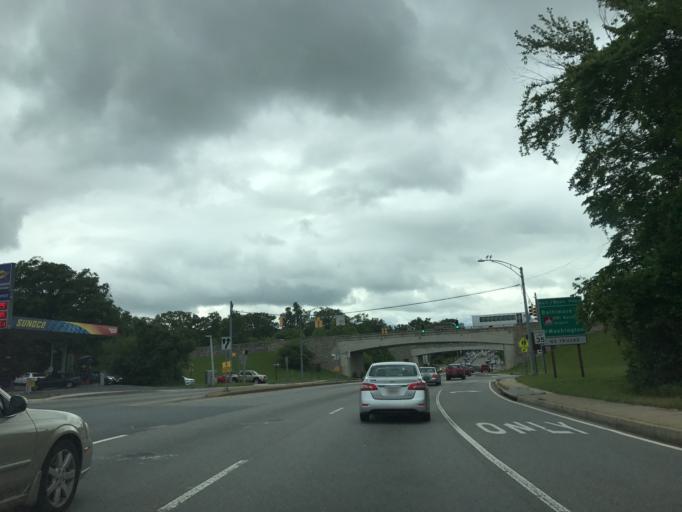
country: US
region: Maryland
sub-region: Prince George's County
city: Woodlawn
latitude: 38.9613
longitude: -76.9034
